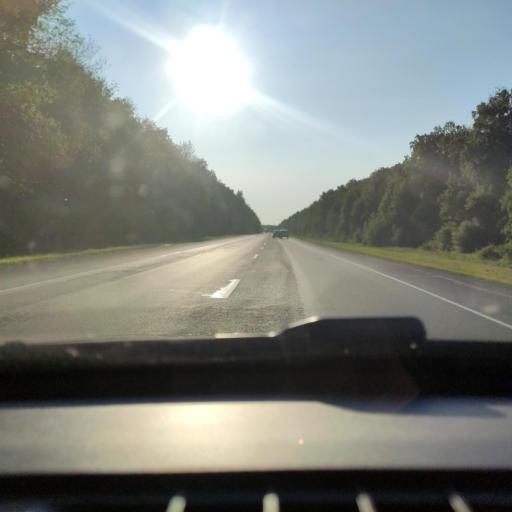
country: RU
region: Voronezj
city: Kashirskoye
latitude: 51.4842
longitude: 39.6558
